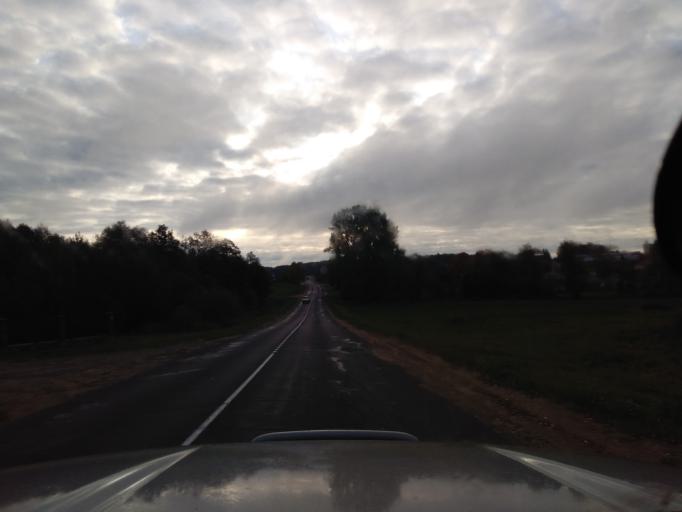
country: BY
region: Minsk
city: Kapyl'
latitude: 53.1607
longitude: 27.0888
